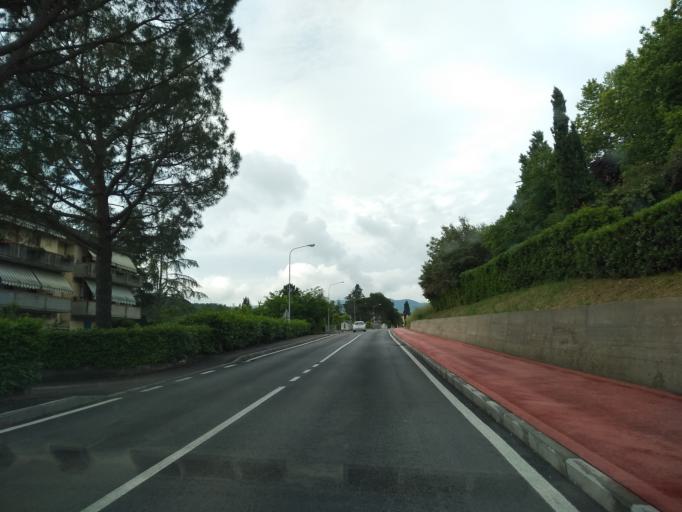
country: IT
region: Tuscany
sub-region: Province of Arezzo
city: Vacchereccia
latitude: 43.5761
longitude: 11.5017
